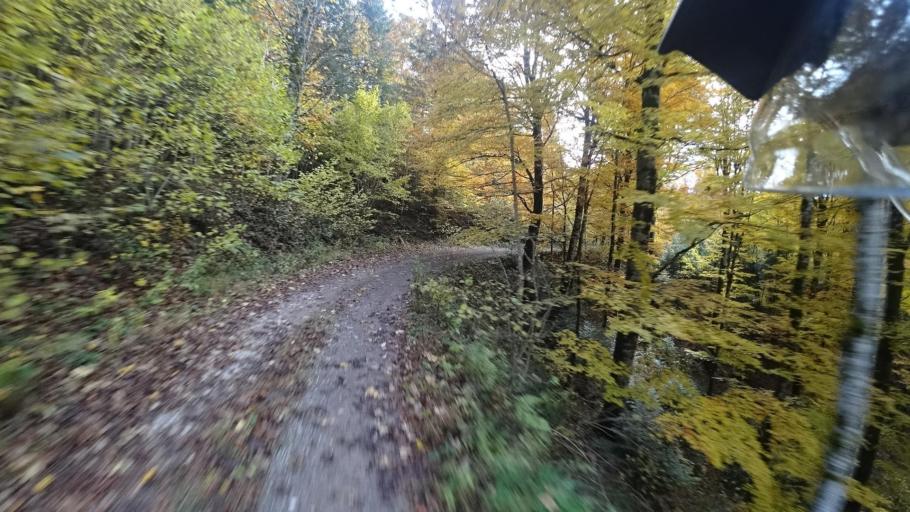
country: HR
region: Karlovacka
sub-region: Grad Ogulin
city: Ogulin
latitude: 45.2059
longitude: 15.1021
